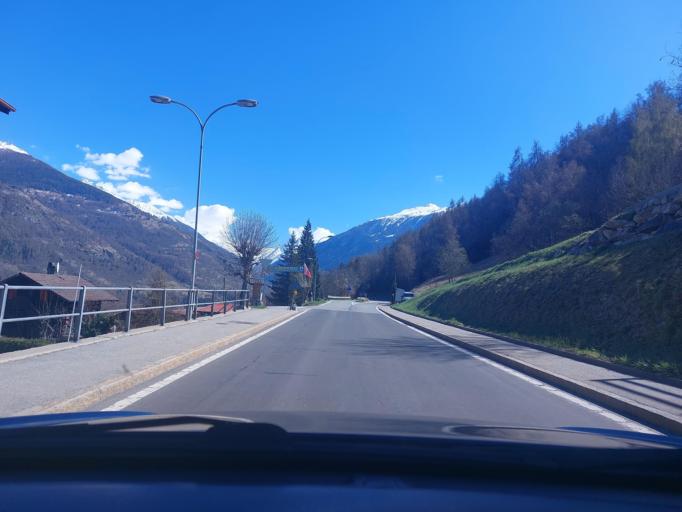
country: CH
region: Valais
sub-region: Herens District
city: Vex
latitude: 46.2074
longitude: 7.4011
